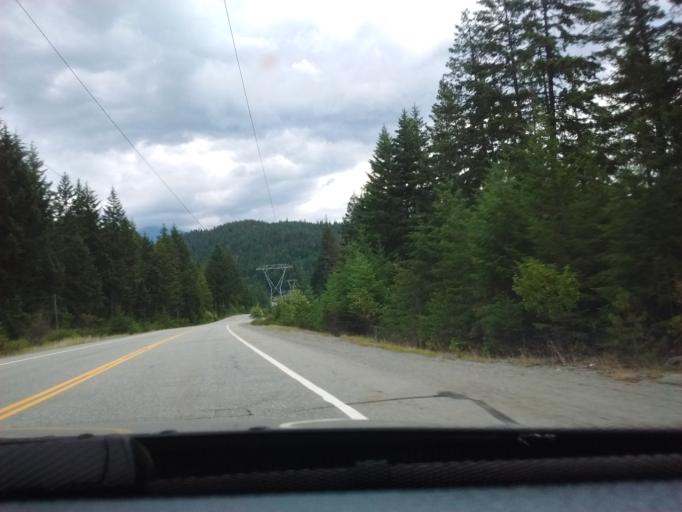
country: CA
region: British Columbia
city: Pemberton
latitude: 50.2962
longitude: -122.8236
